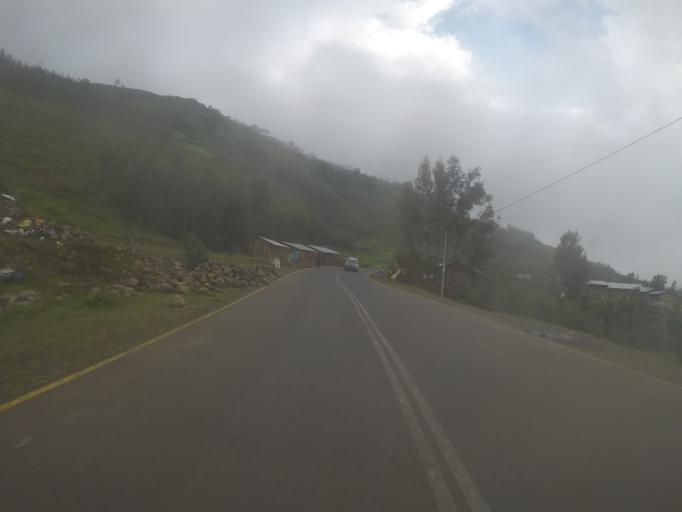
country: ET
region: Amhara
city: Gondar
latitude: 12.7259
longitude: 37.5110
